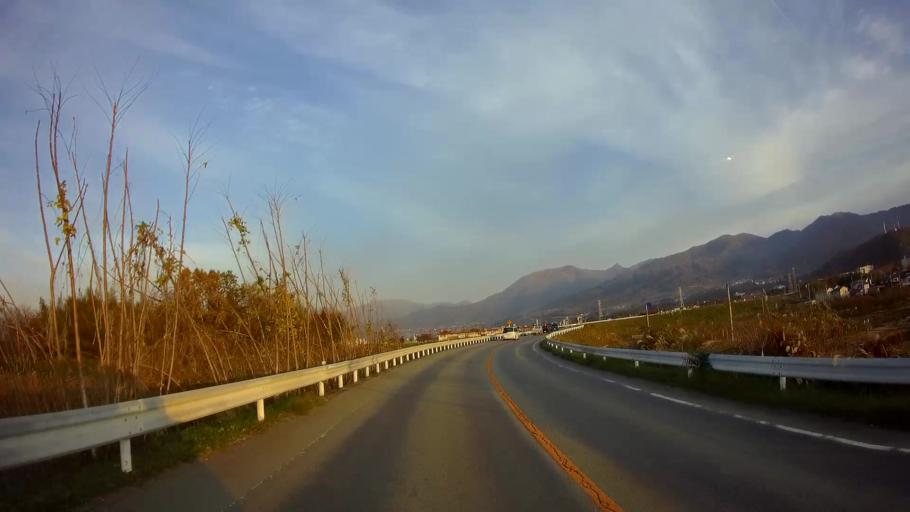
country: JP
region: Yamanashi
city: Isawa
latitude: 35.6123
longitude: 138.6034
